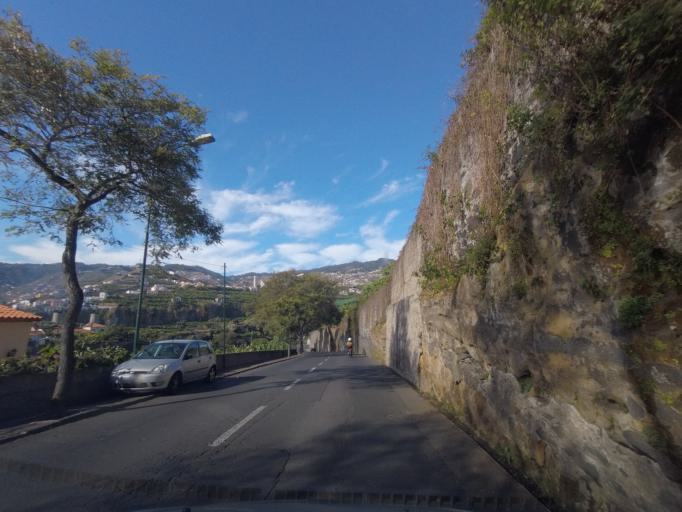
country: PT
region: Madeira
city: Camara de Lobos
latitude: 32.6457
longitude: -16.9653
